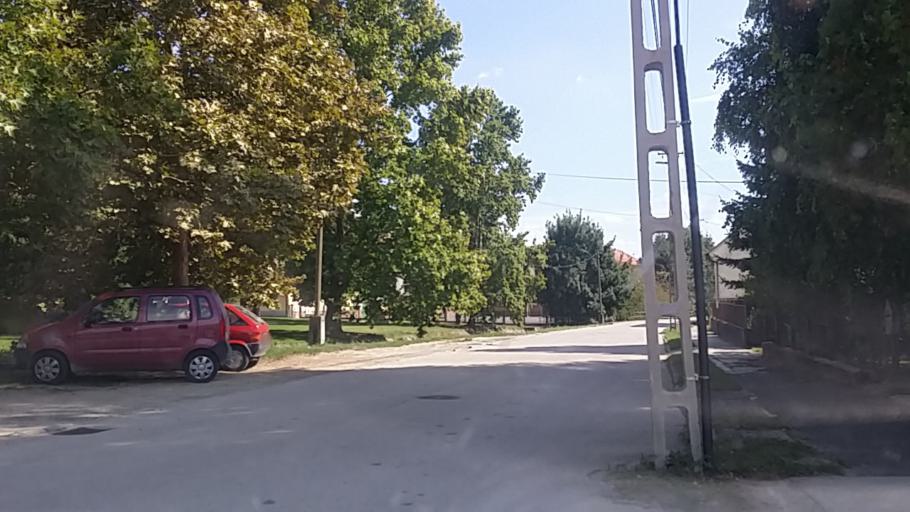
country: HU
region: Tolna
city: Gyonk
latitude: 46.5576
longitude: 18.4775
